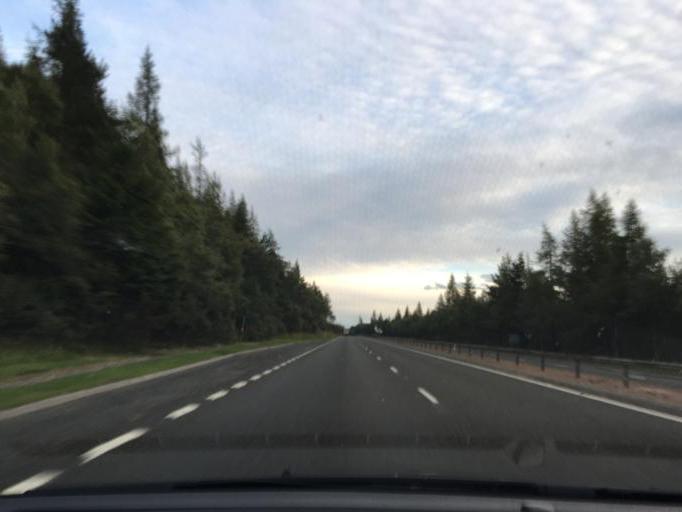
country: GB
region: Scotland
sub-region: Highland
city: Aviemore
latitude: 57.3287
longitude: -3.9781
